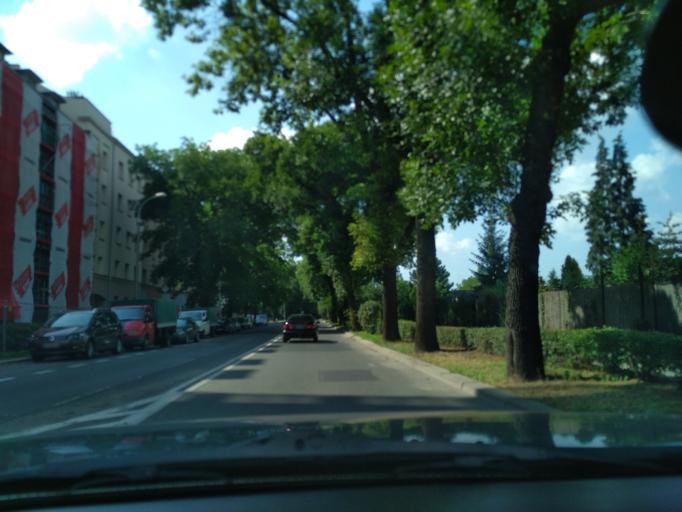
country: PL
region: Silesian Voivodeship
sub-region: Gliwice
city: Gliwice
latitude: 50.2979
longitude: 18.6641
